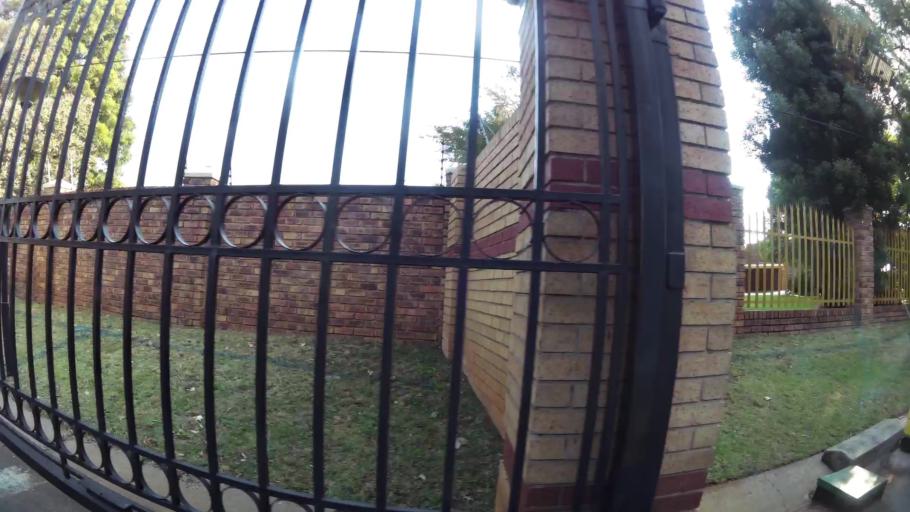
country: ZA
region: Gauteng
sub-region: City of Johannesburg Metropolitan Municipality
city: Modderfontein
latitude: -26.0780
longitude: 28.2046
